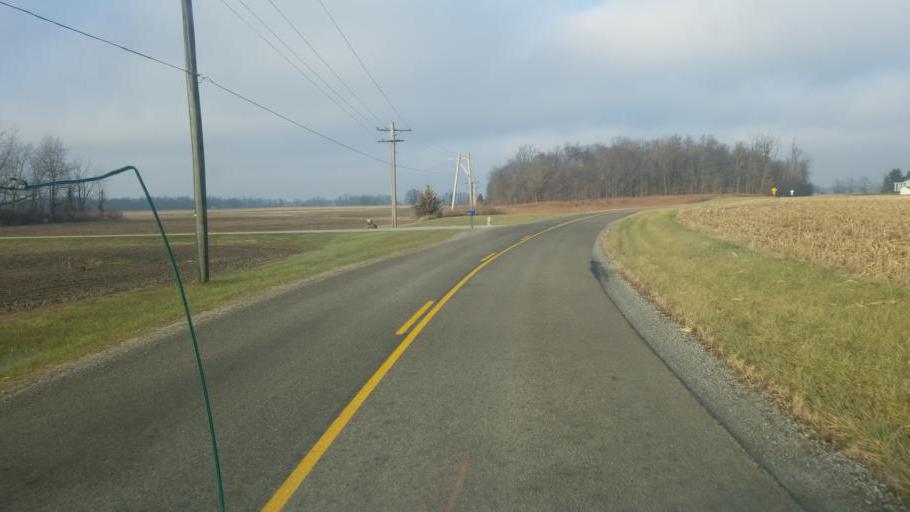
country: US
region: Ohio
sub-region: Hardin County
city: Kenton
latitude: 40.6836
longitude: -83.5761
